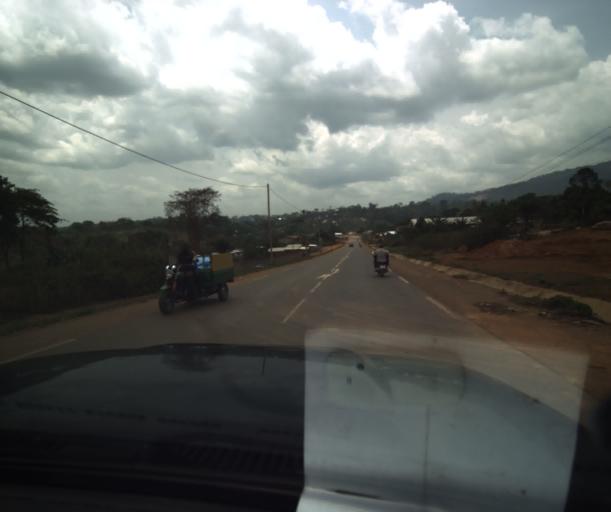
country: CM
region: Centre
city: Mbankomo
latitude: 3.8014
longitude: 11.4578
